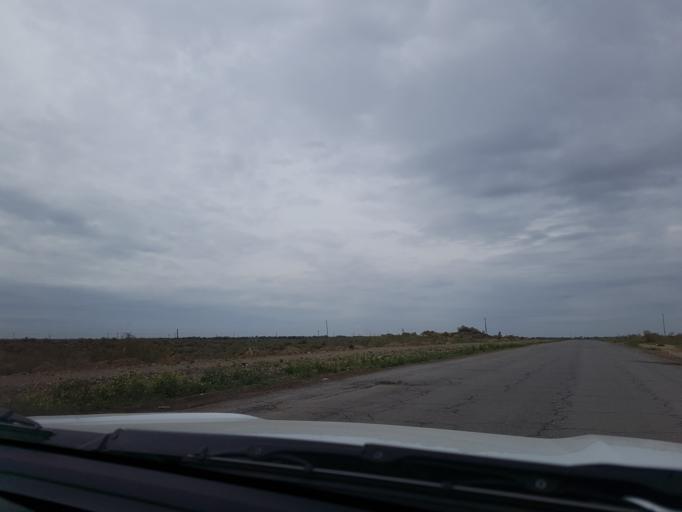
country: TM
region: Mary
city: Bayramaly
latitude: 37.8045
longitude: 62.5633
